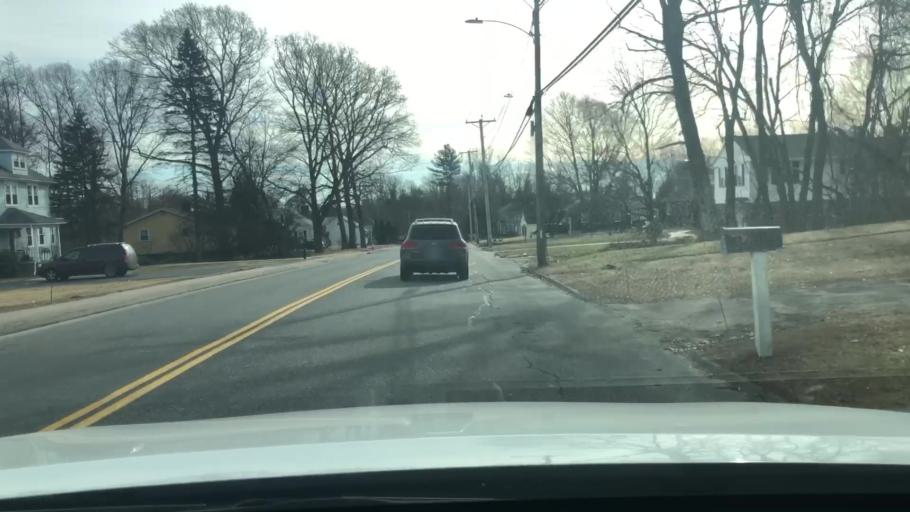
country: US
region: Massachusetts
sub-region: Worcester County
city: Hopedale
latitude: 42.1434
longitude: -71.5368
